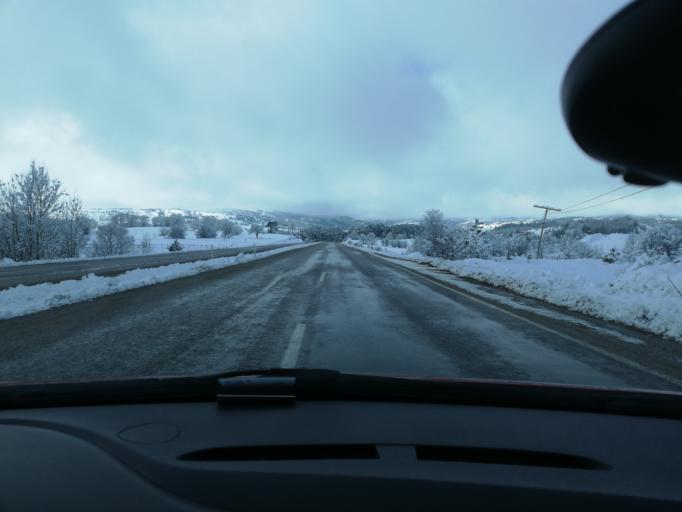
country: TR
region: Kastamonu
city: Ihsangazi
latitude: 41.3161
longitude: 33.6015
